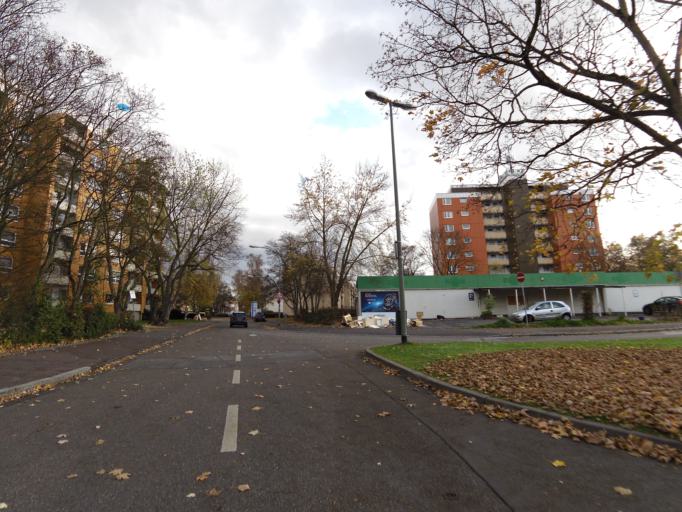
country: DE
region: Hesse
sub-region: Regierungsbezirk Darmstadt
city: Eschborn
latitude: 50.0974
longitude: 8.5718
